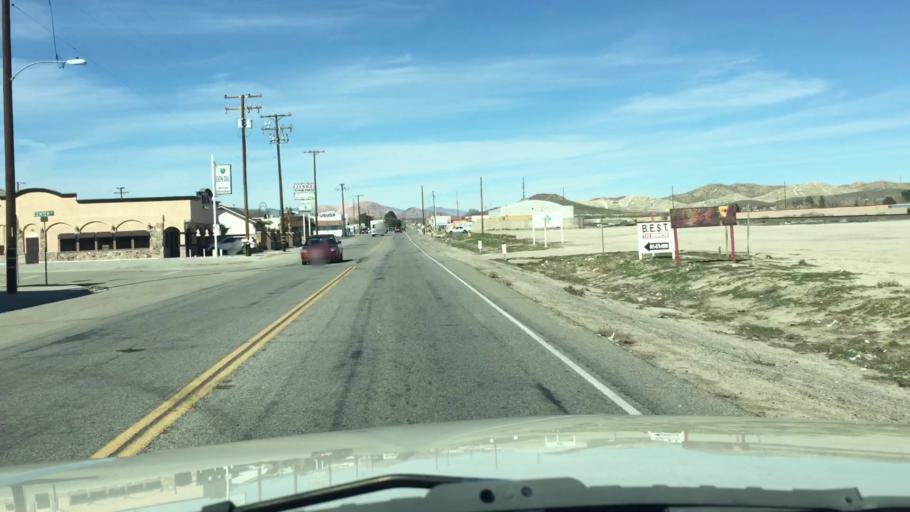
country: US
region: California
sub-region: Kern County
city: Rosamond
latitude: 34.8596
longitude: -118.1625
